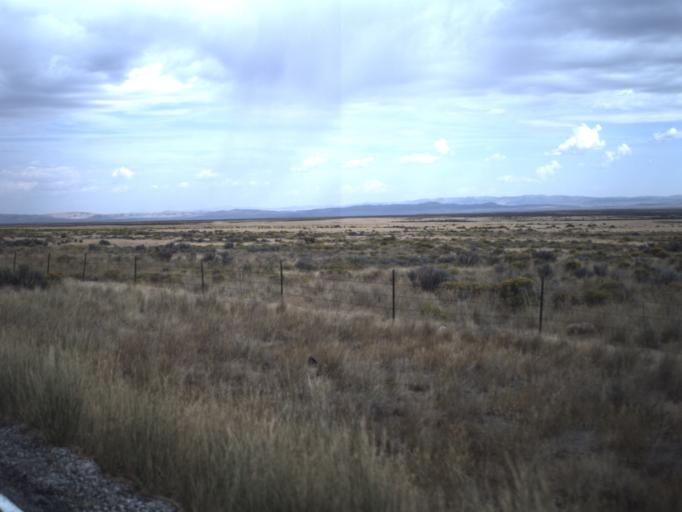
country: US
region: Idaho
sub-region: Oneida County
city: Malad City
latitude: 41.8937
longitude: -113.1103
